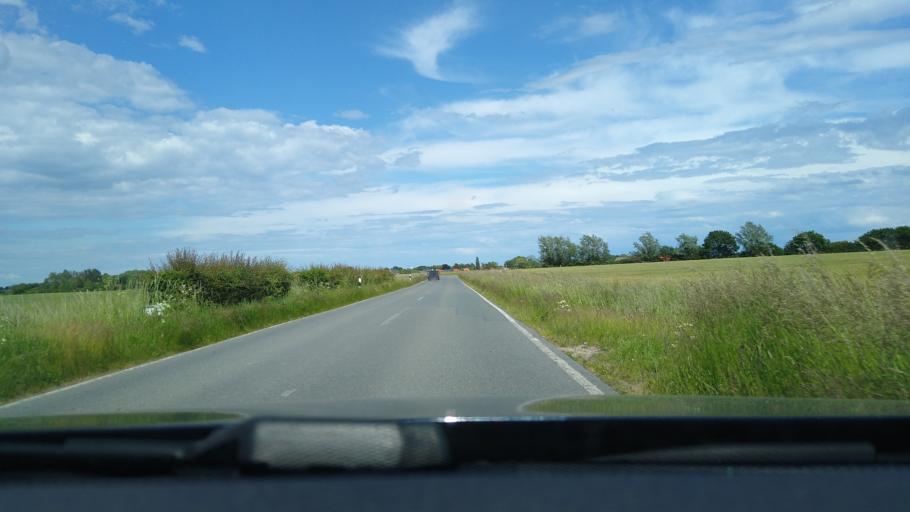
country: DE
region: Schleswig-Holstein
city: Grube
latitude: 54.2280
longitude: 11.0232
